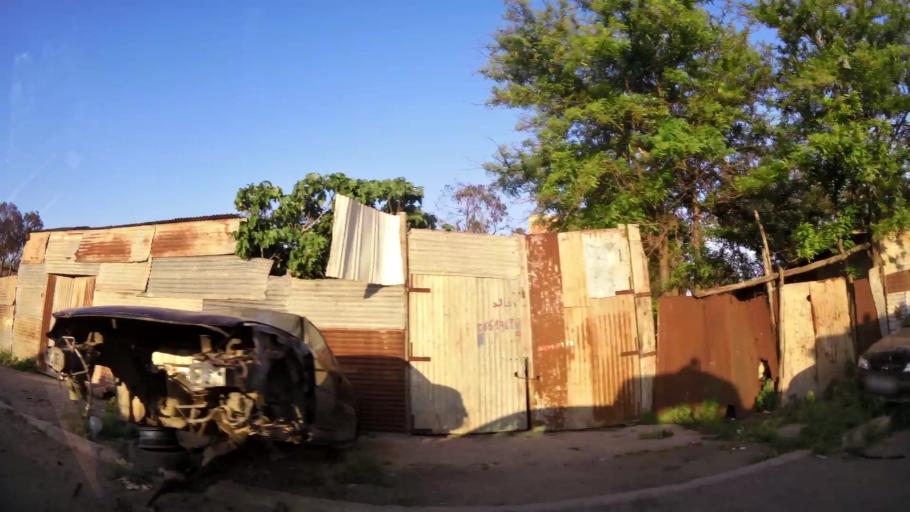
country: MA
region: Oriental
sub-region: Oujda-Angad
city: Oujda
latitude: 34.7122
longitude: -1.9112
